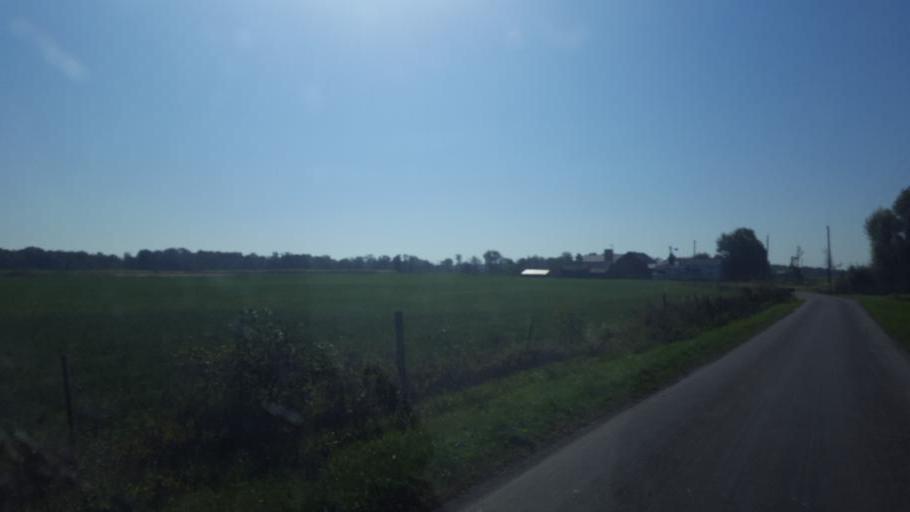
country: US
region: Ohio
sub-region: Hardin County
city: Kenton
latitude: 40.6047
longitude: -83.5561
